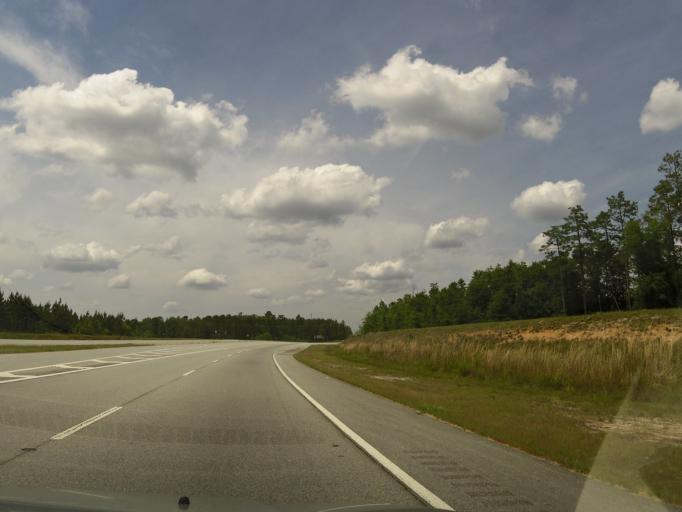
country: US
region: Georgia
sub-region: Emanuel County
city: Swainsboro
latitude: 32.6712
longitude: -82.3844
